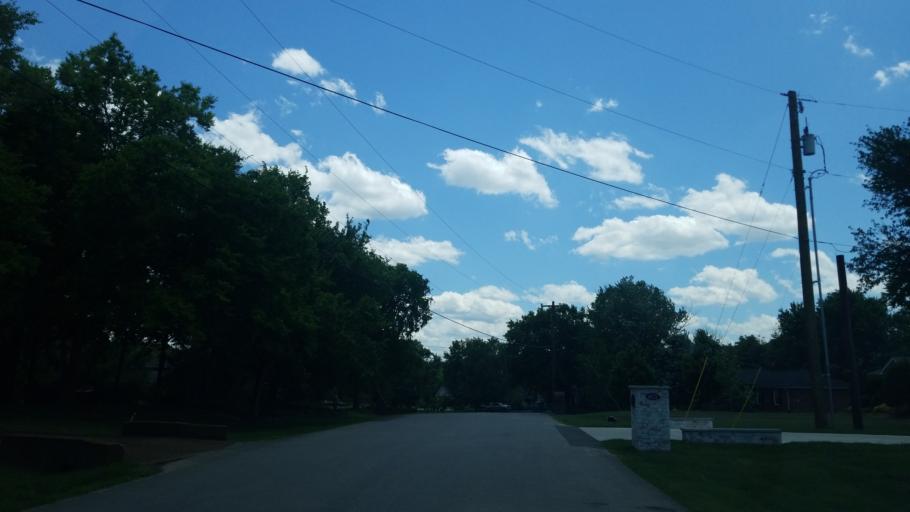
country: US
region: Tennessee
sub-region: Davidson County
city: Forest Hills
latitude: 36.0336
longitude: -86.8266
